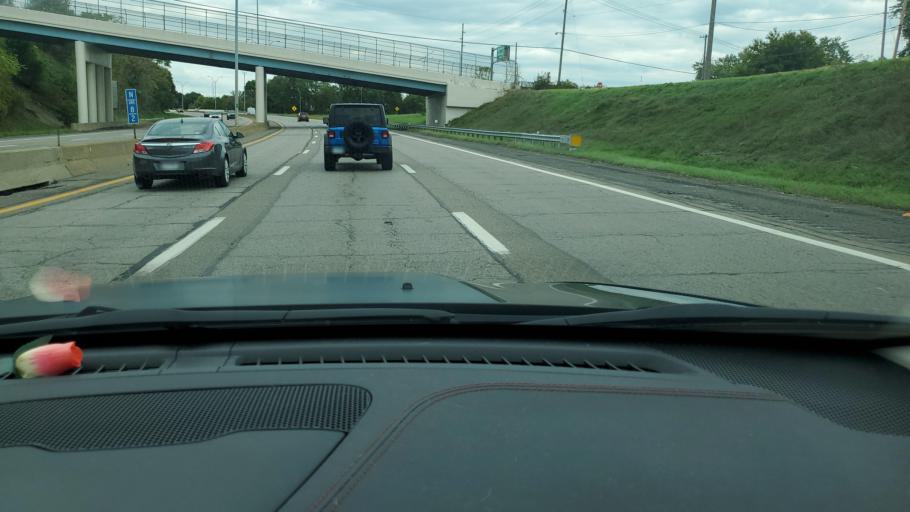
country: US
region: Ohio
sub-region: Mahoning County
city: Campbell
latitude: 41.0751
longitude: -80.6267
